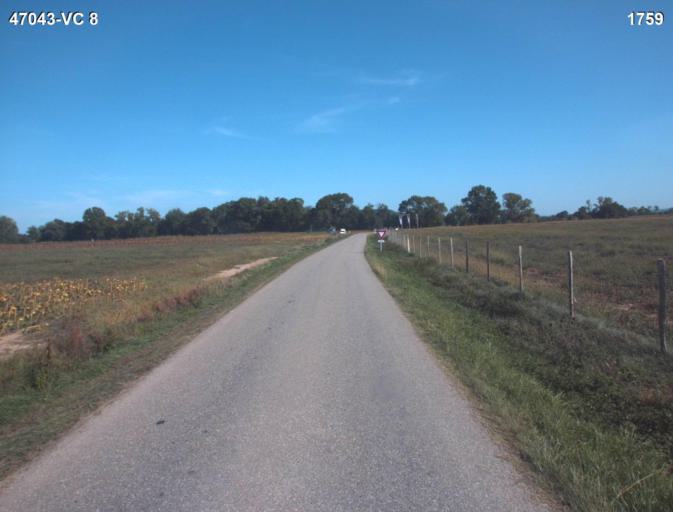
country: FR
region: Aquitaine
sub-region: Departement du Lot-et-Garonne
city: Buzet-sur-Baise
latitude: 44.2782
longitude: 0.3001
